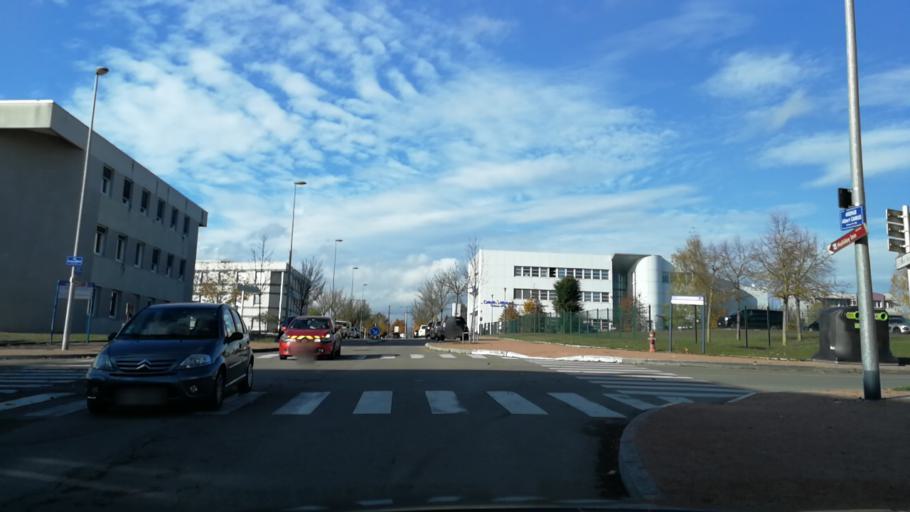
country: FR
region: Bourgogne
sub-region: Departement de la Cote-d'Or
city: Fontaine-les-Dijon
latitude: 47.3528
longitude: 5.0480
